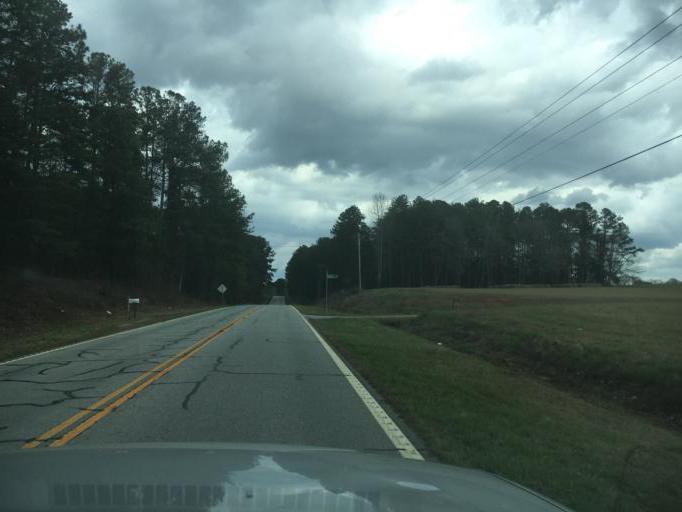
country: US
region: South Carolina
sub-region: Oconee County
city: Westminster
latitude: 34.7079
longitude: -83.0725
